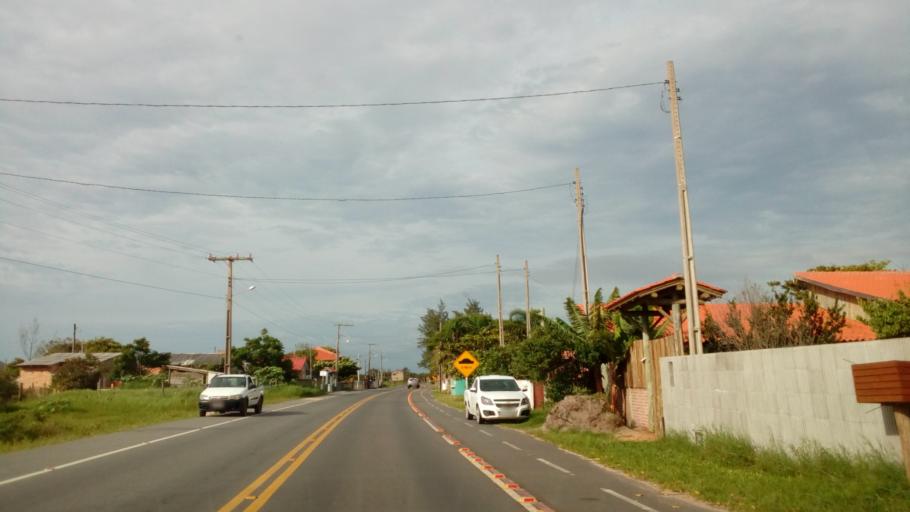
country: BR
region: Santa Catarina
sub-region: Laguna
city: Laguna
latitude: -28.5695
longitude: -48.8128
